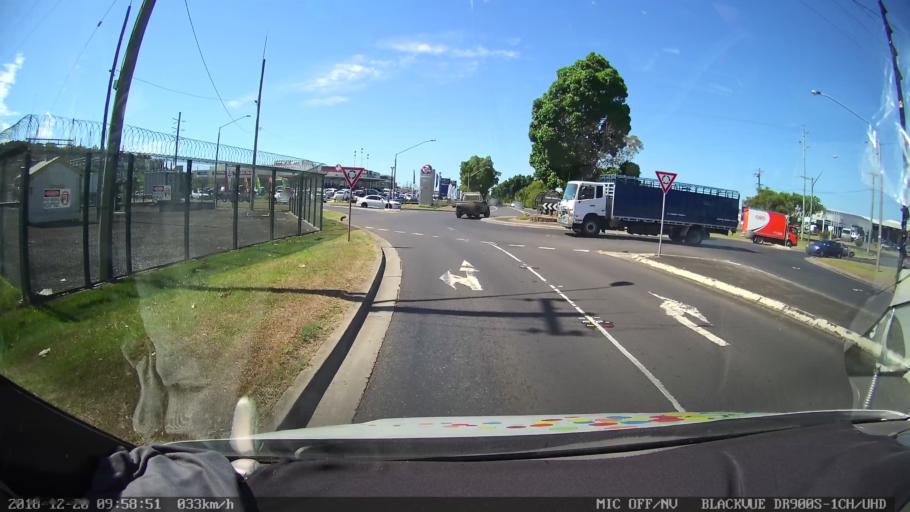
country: AU
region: New South Wales
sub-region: Lismore Municipality
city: Lismore
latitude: -28.8207
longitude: 153.2653
